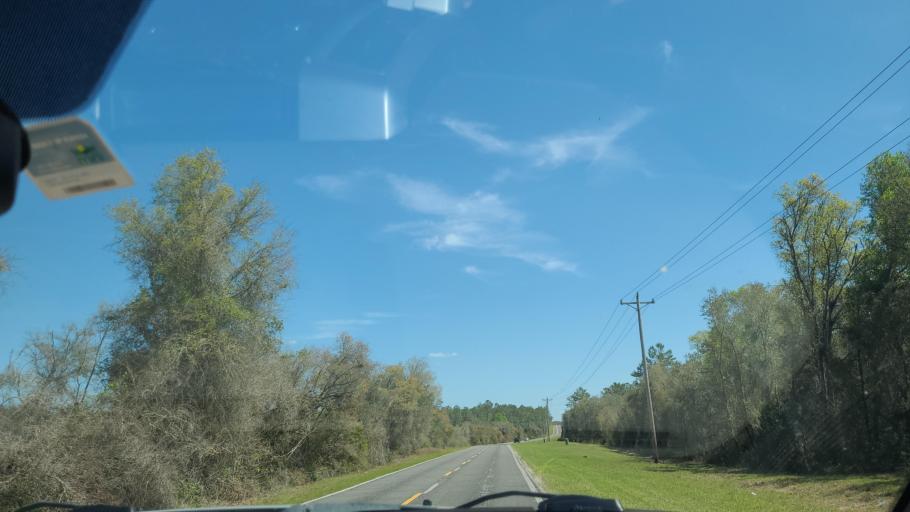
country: US
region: Florida
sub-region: Marion County
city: Citra
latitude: 29.4109
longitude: -81.9068
